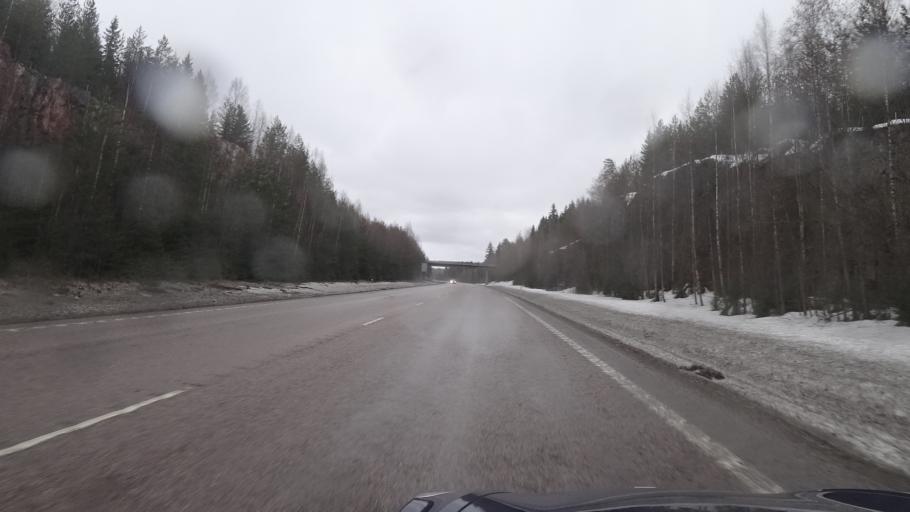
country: FI
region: Paijanne Tavastia
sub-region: Lahti
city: Nastola
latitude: 60.9317
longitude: 25.9238
